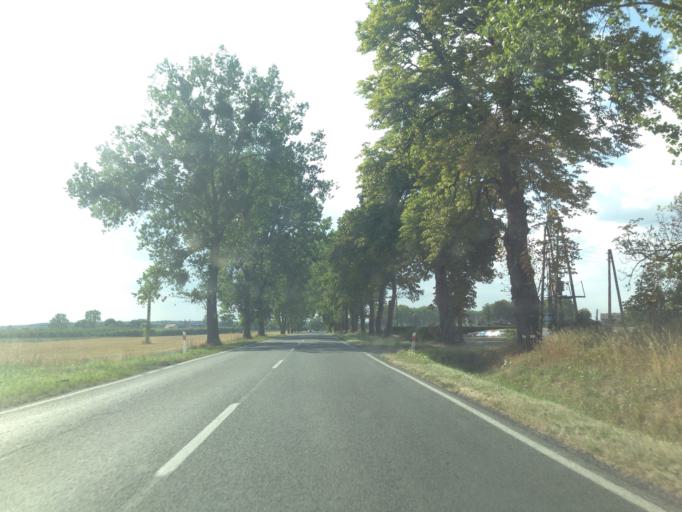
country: PL
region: Kujawsko-Pomorskie
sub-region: Powiat swiecki
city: Bukowiec
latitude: 53.4537
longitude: 18.2107
